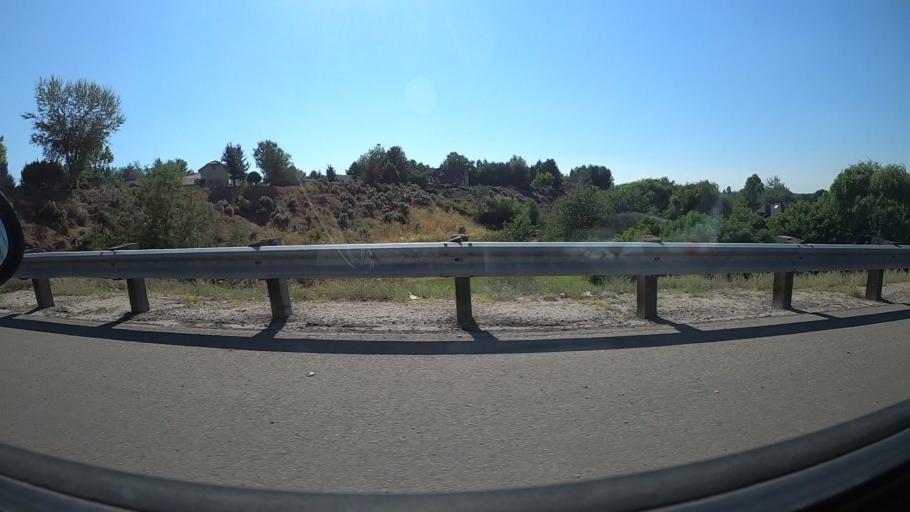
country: US
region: Idaho
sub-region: Ada County
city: Eagle
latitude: 43.6664
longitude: -116.3545
